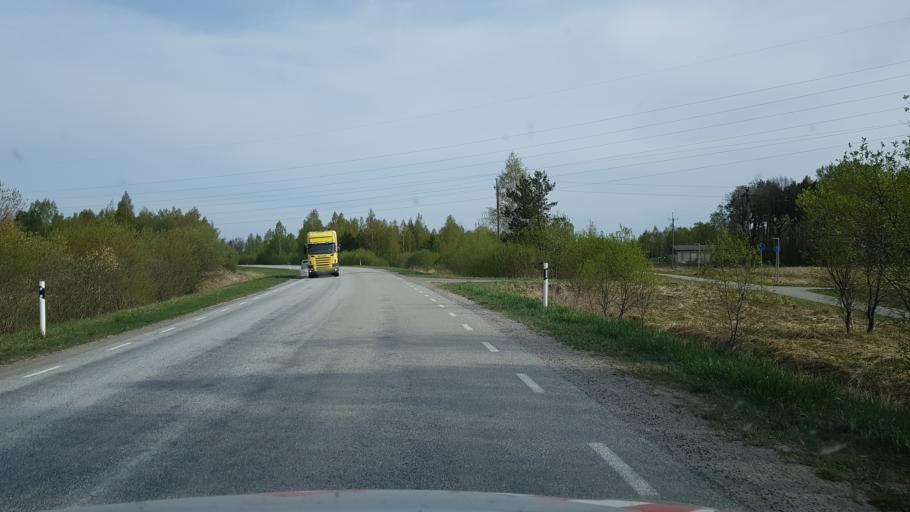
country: EE
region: Paernumaa
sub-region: Audru vald
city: Audru
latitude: 58.4165
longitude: 24.3116
